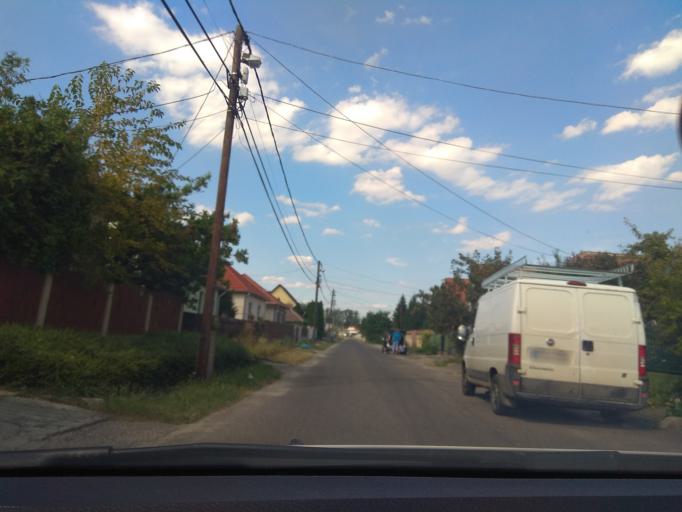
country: HU
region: Borsod-Abauj-Zemplen
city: Miskolc
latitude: 48.0571
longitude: 20.7949
